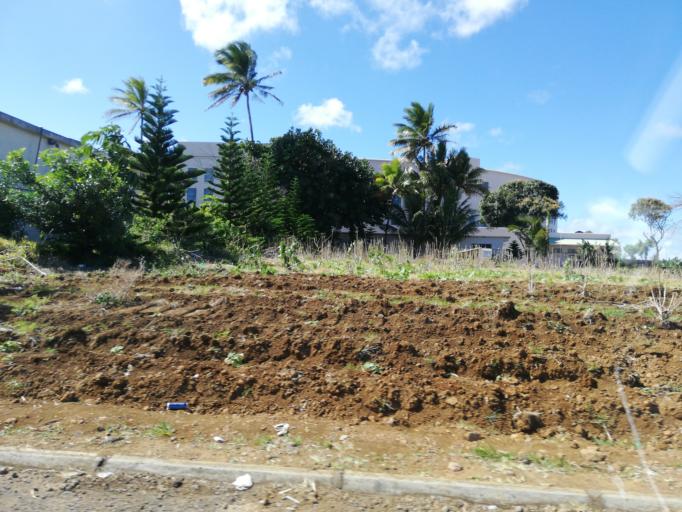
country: MU
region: Grand Port
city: Plaine Magnien
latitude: -20.4414
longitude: 57.6709
